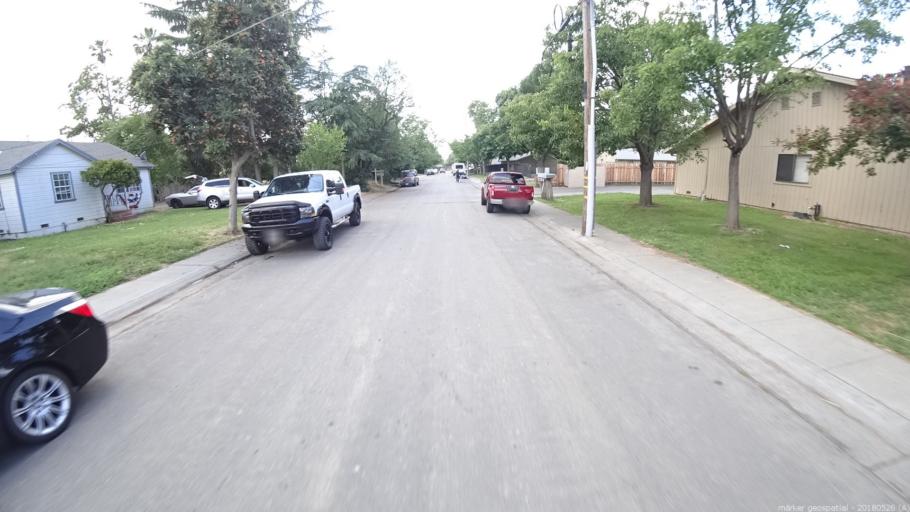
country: US
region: California
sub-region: Sacramento County
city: Sacramento
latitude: 38.6139
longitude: -121.4739
